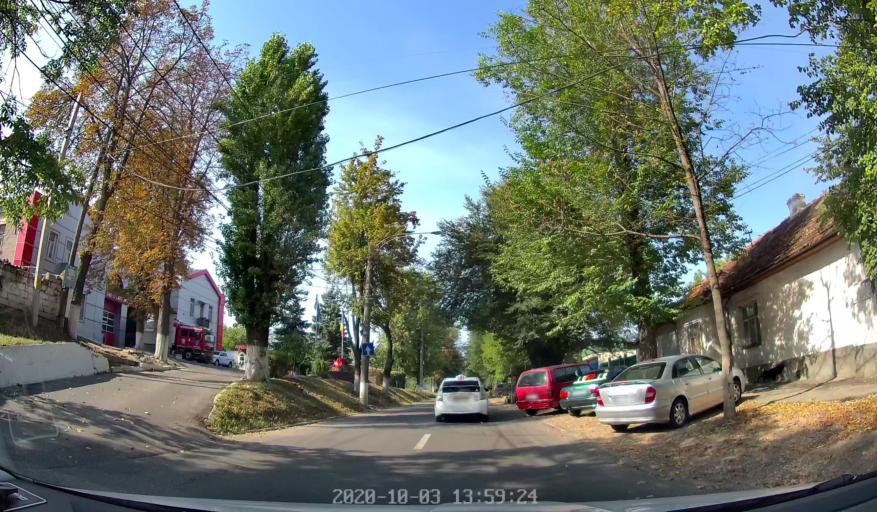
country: MD
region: Chisinau
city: Chisinau
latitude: 47.0106
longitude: 28.8339
